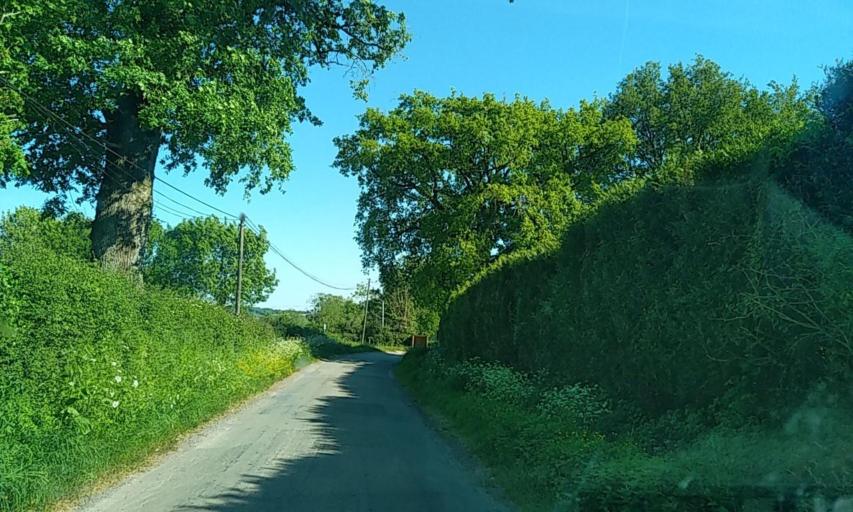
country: FR
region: Poitou-Charentes
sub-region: Departement des Deux-Sevres
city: Boisme
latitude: 46.7845
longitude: -0.4168
